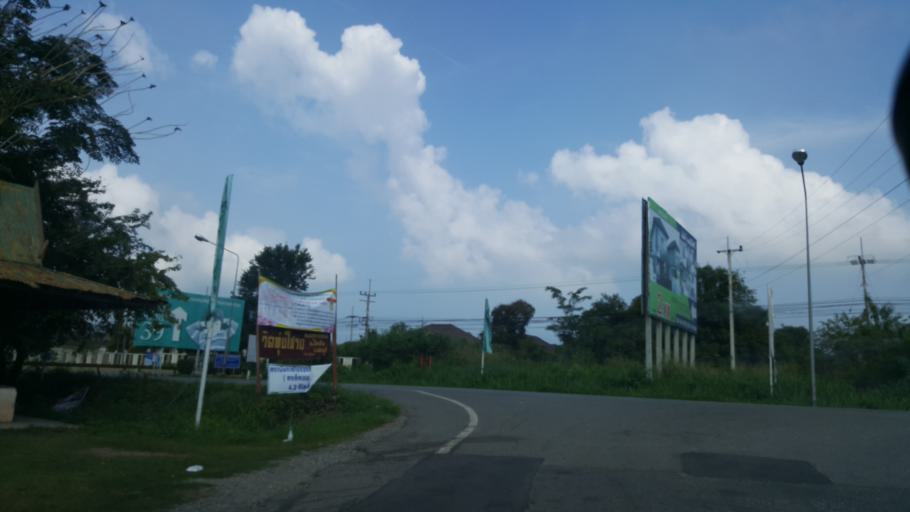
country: TH
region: Chon Buri
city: Sattahip
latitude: 12.7314
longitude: 100.9123
